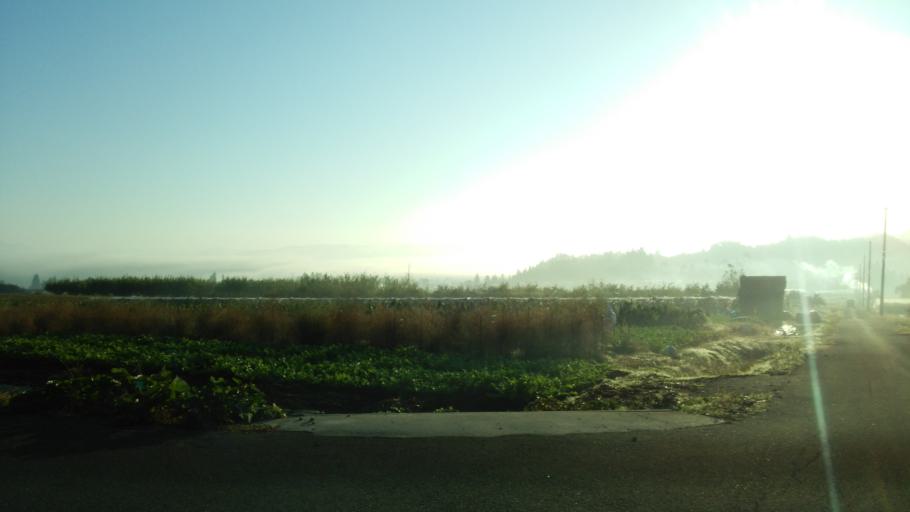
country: JP
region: Fukushima
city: Kitakata
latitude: 37.4332
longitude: 139.8004
